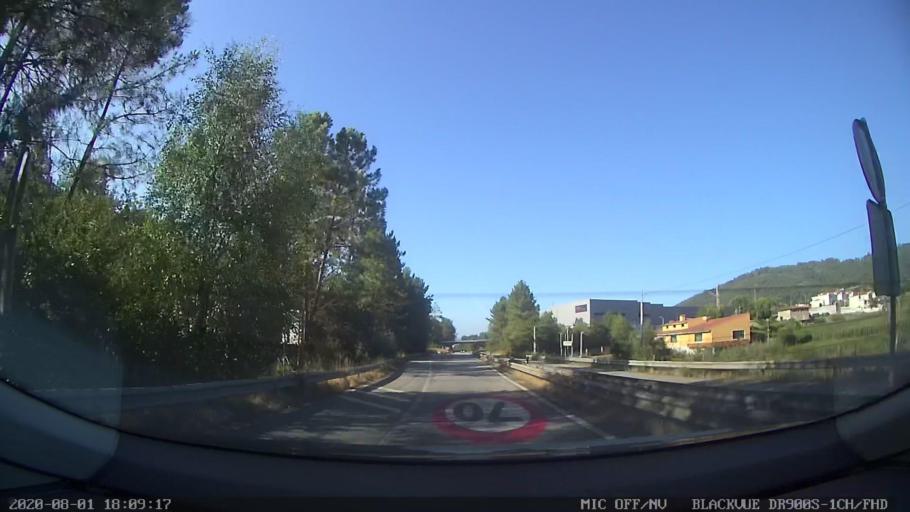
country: PT
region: Porto
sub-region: Santo Tirso
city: Sao Miguel do Couto
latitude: 41.3134
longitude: -8.4705
